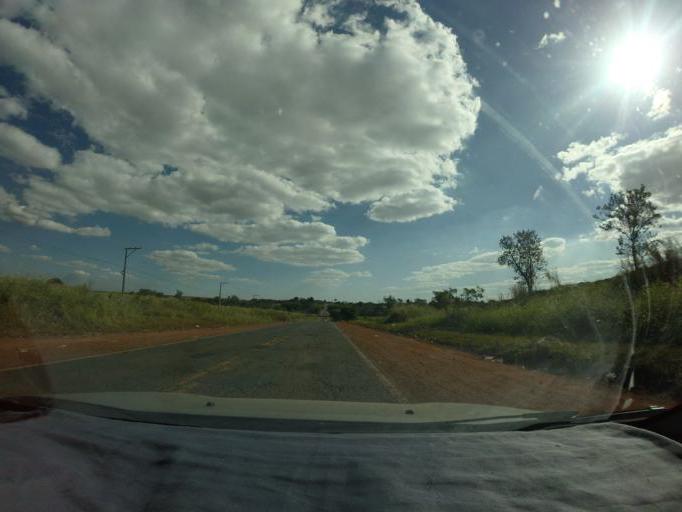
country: BR
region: Sao Paulo
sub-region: Piracicaba
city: Piracicaba
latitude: -22.7340
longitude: -47.5536
